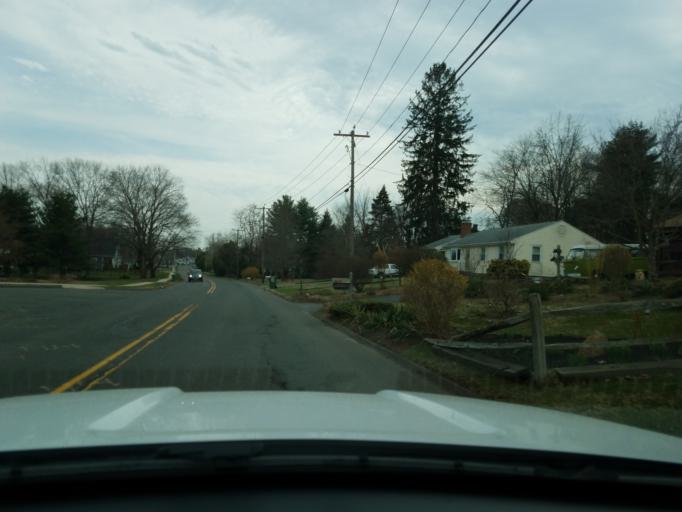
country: US
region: Connecticut
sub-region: Middlesex County
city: Cromwell
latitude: 41.6179
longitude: -72.6684
